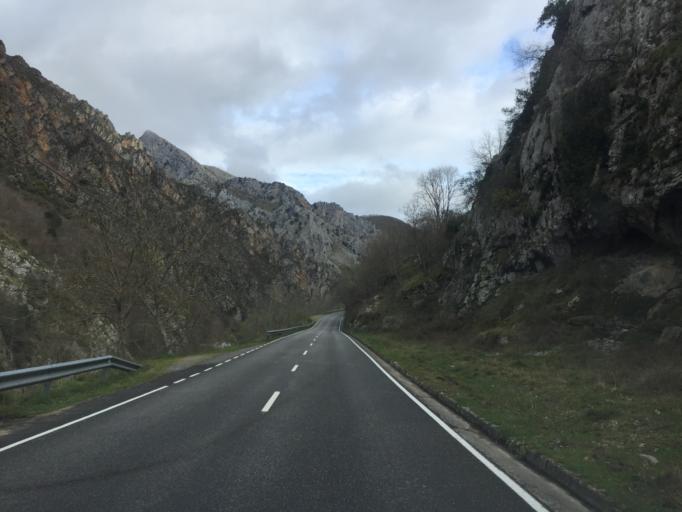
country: ES
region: Asturias
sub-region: Province of Asturias
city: Carrena
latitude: 43.2717
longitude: -4.8323
